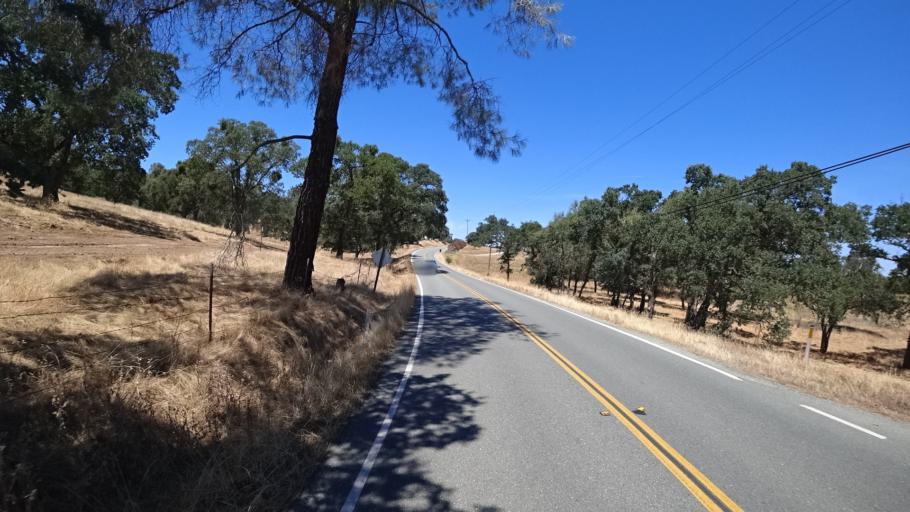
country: US
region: California
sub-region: Calaveras County
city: Valley Springs
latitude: 38.2069
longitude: -120.8274
